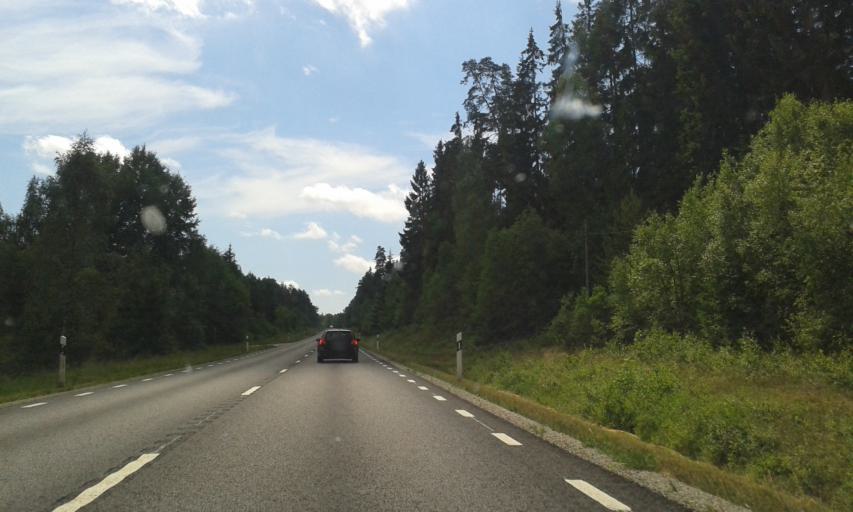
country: SE
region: Joenkoeping
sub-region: Varnamo Kommun
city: Rydaholm
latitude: 57.0155
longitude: 14.2597
